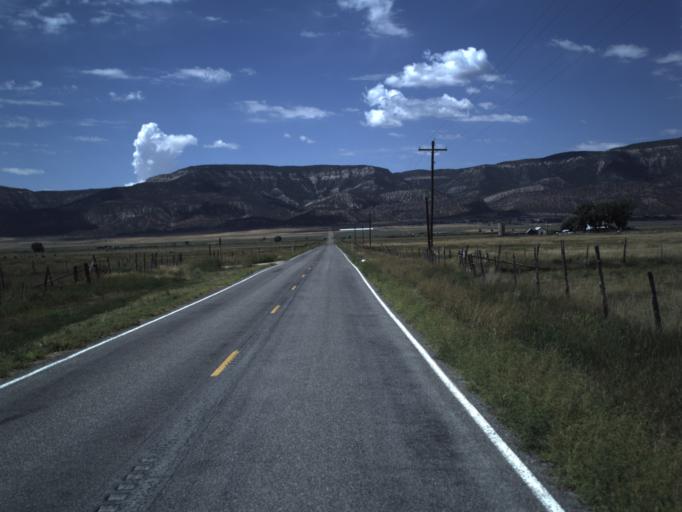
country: US
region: Utah
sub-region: Sanpete County
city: Moroni
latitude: 39.4759
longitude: -111.5811
